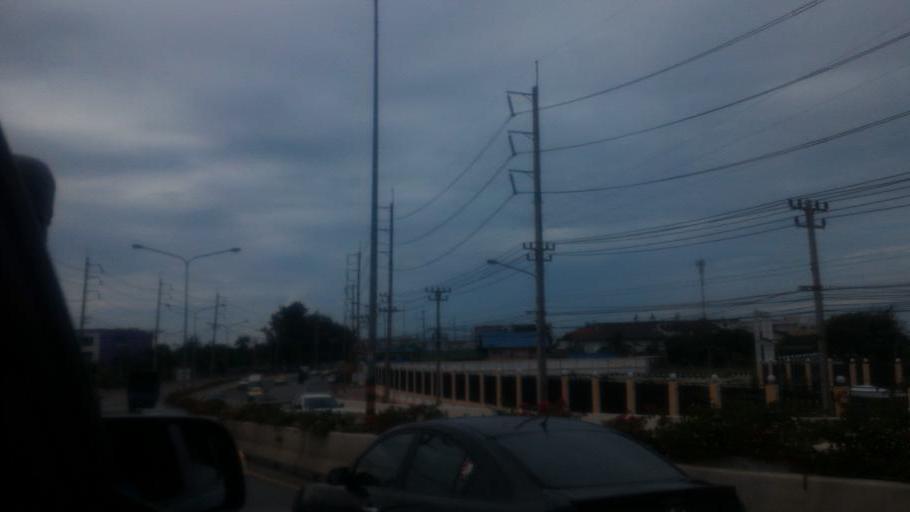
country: TH
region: Bangkok
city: Bang Khun Thian
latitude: 13.6230
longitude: 100.4371
